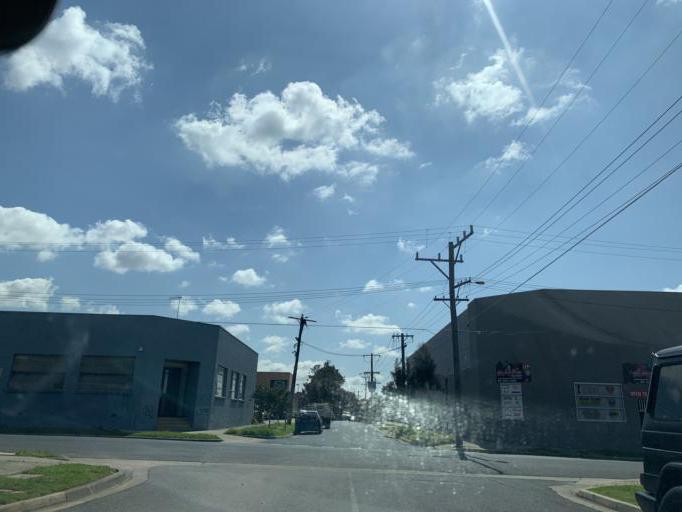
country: AU
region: Victoria
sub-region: Moreland
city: Coburg North
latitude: -37.7263
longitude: 144.9516
